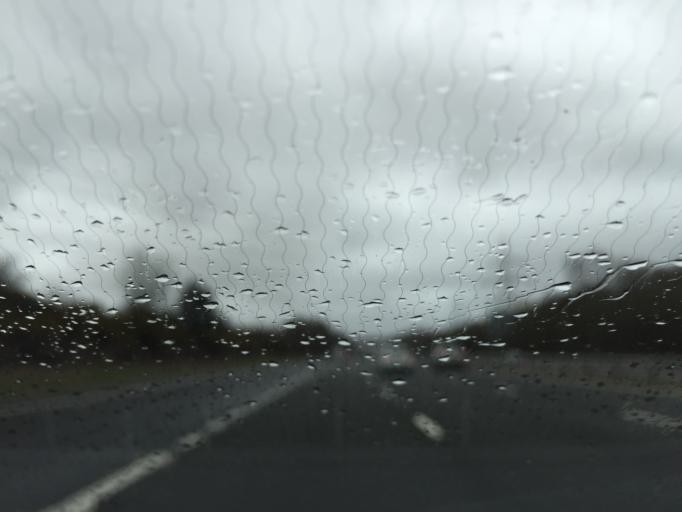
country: GB
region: England
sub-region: Hampshire
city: Totton
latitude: 50.9464
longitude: -1.5239
